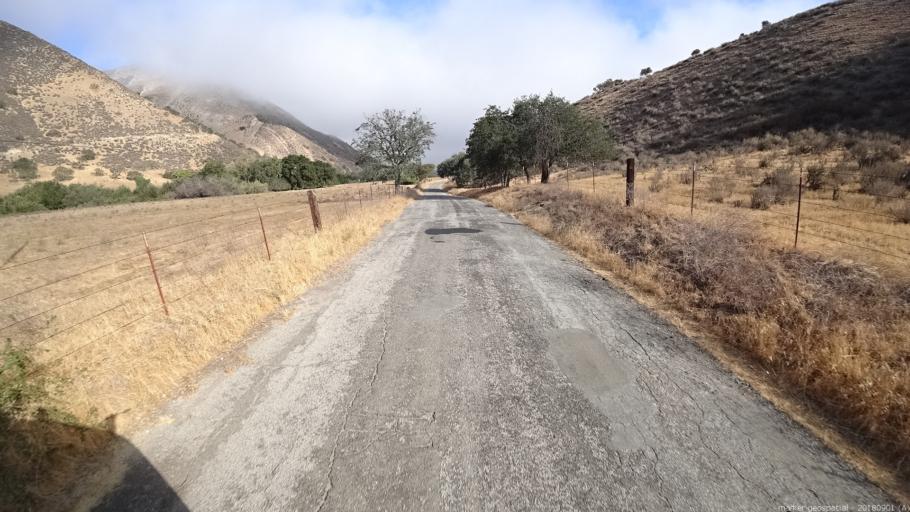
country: US
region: California
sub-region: Monterey County
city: Greenfield
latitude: 36.2592
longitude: -121.2943
